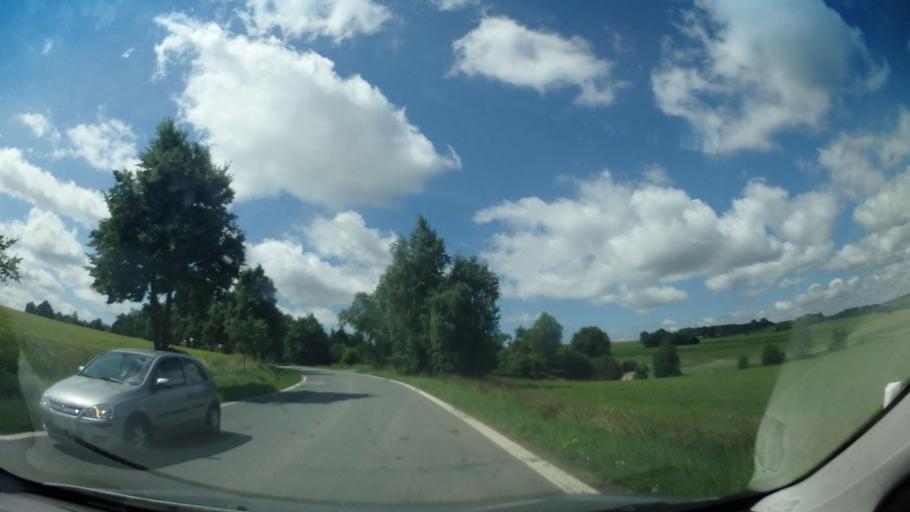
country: CZ
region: Vysocina
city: Zd'ar nad Sazavou Druhy
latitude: 49.5861
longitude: 15.9688
